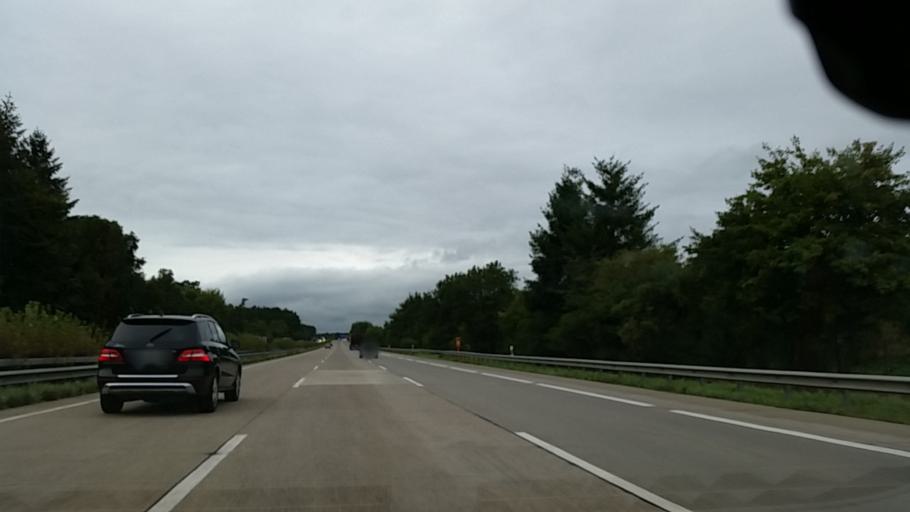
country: DE
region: Lower Saxony
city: Brackel
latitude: 53.3215
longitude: 10.0576
